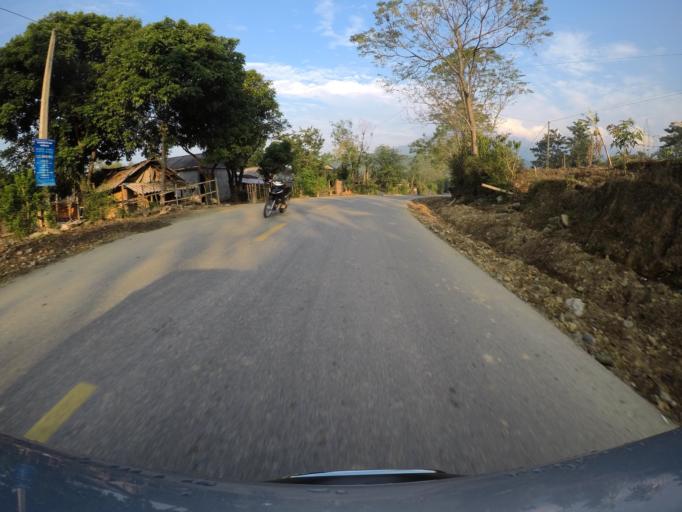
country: VN
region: Lai Chau
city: Tam Duong
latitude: 22.3009
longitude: 103.6683
